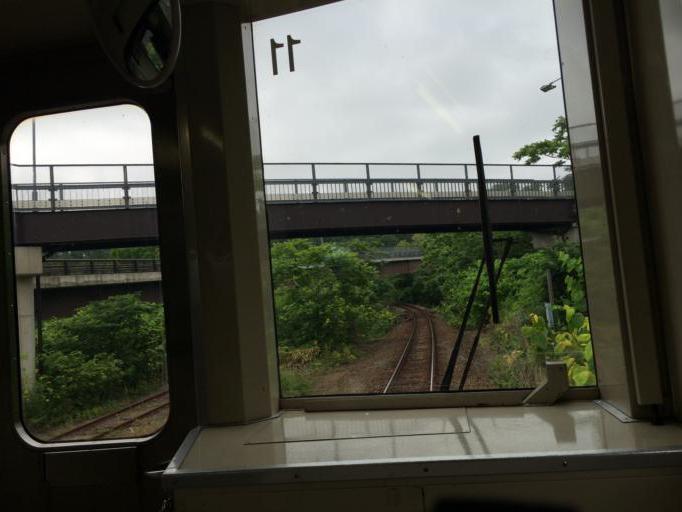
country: JP
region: Hokkaido
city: Otaru
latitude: 43.2030
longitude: 140.9277
